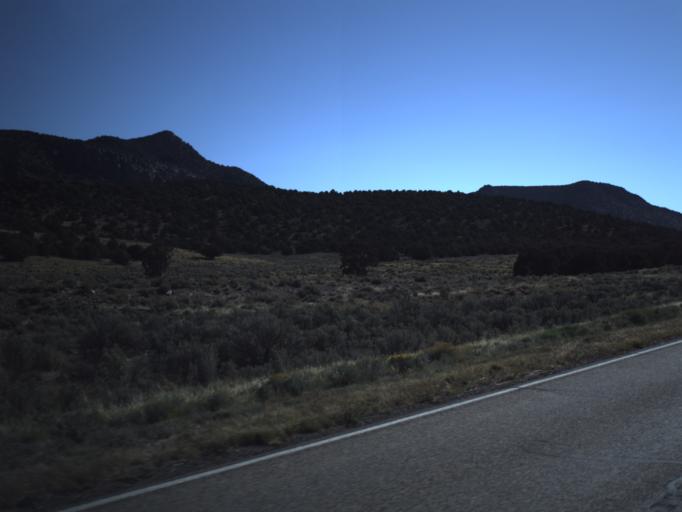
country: US
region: Utah
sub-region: Washington County
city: Enterprise
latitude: 37.6728
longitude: -113.4892
